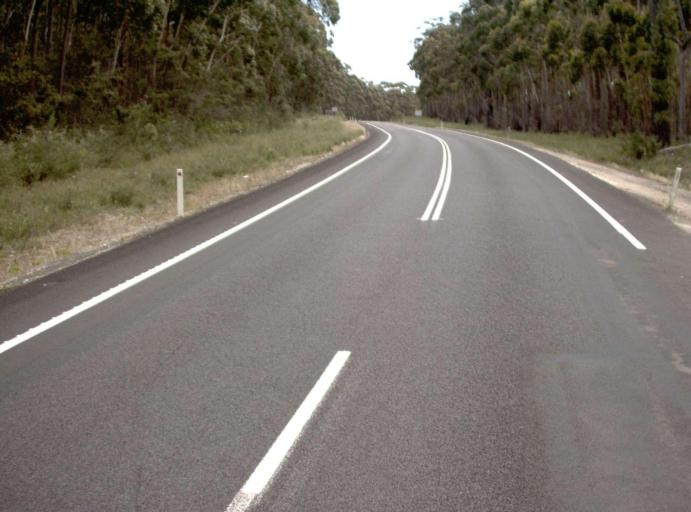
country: AU
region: New South Wales
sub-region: Bega Valley
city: Eden
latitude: -37.5093
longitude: 149.5161
